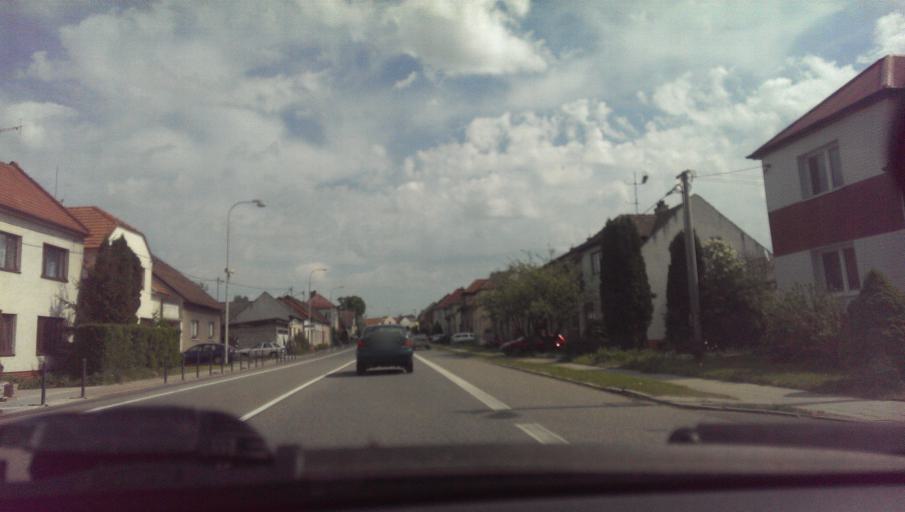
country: CZ
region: Zlin
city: Spytihnev
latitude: 49.1359
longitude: 17.4899
